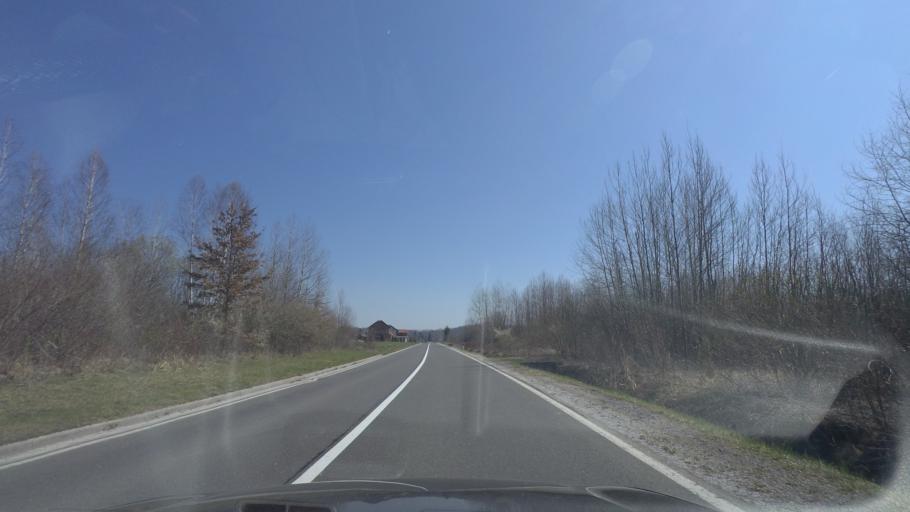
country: HR
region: Sisacko-Moslavacka
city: Gvozd
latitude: 45.3231
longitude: 15.9443
